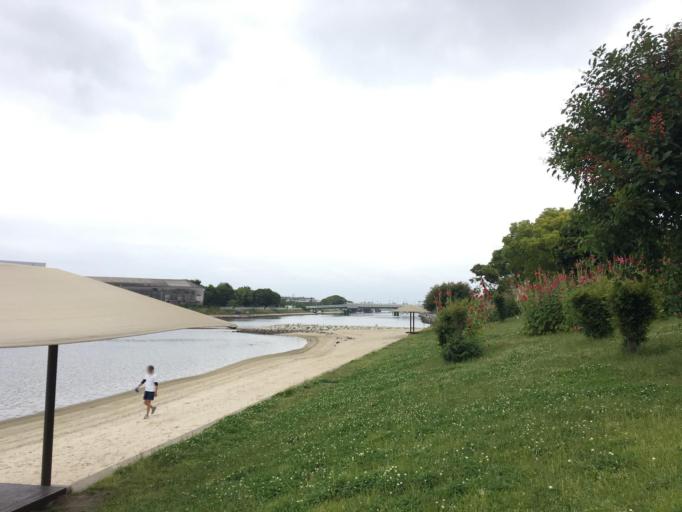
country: JP
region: Kanagawa
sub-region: Kawasaki-shi
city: Kawasaki
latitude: 35.5720
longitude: 139.7431
